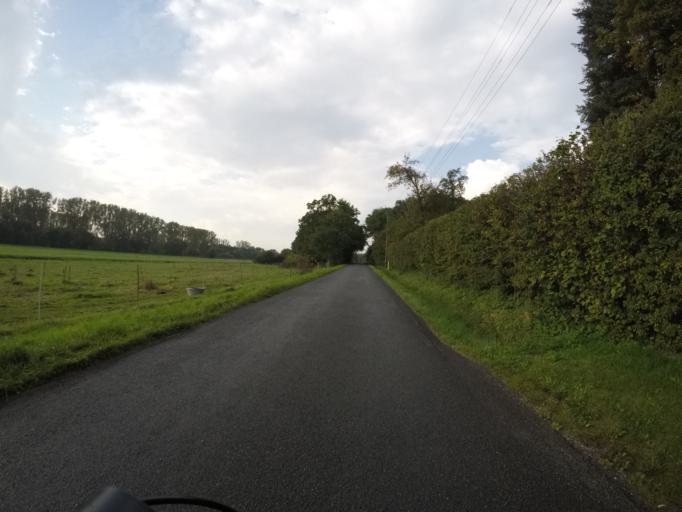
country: DE
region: North Rhine-Westphalia
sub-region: Regierungsbezirk Detmold
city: Bielefeld
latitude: 52.0467
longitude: 8.6135
